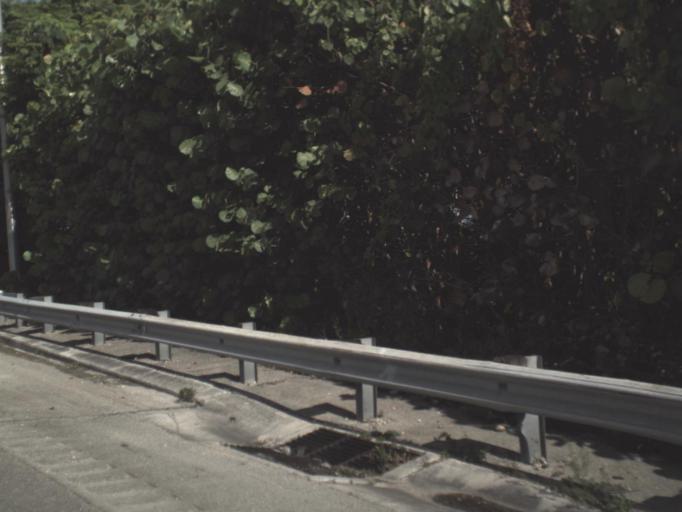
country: US
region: Florida
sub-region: Broward County
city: Pembroke Pines
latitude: 25.9947
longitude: -80.2247
